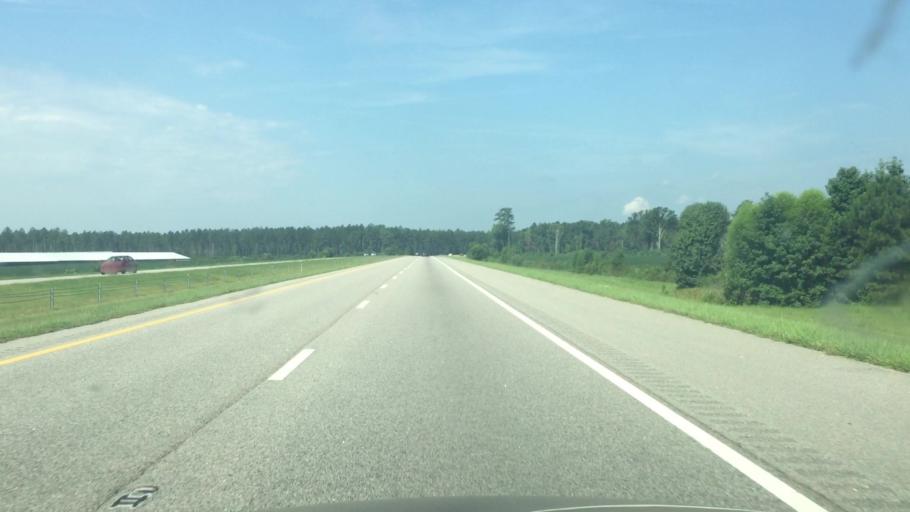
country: US
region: North Carolina
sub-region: Robeson County
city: Pembroke
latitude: 34.5953
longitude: -79.1735
